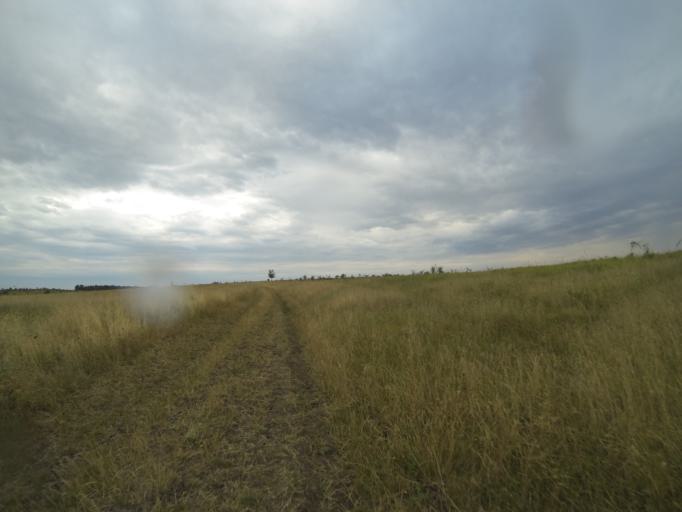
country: RO
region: Dolj
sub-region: Comuna Bradesti
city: Bradesti
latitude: 44.5531
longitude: 23.6405
